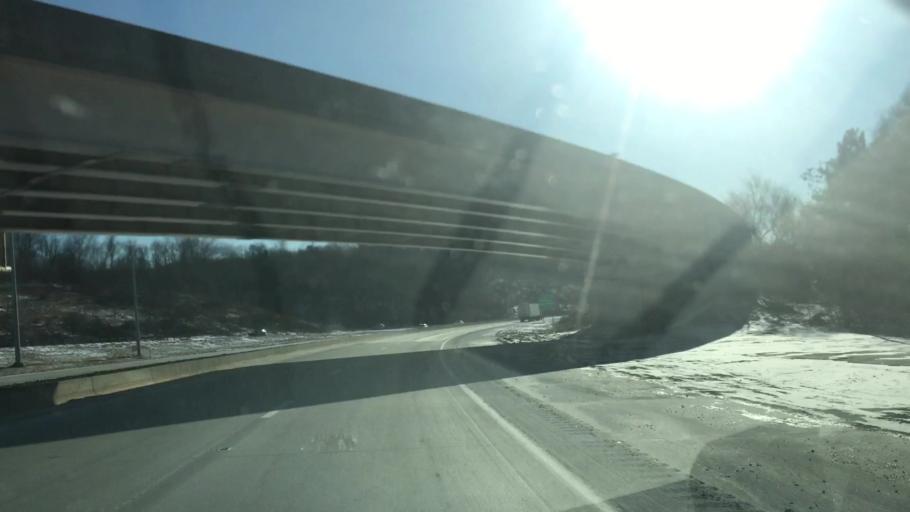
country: US
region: Pennsylvania
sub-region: Allegheny County
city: Enlow
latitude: 40.4660
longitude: -80.1998
